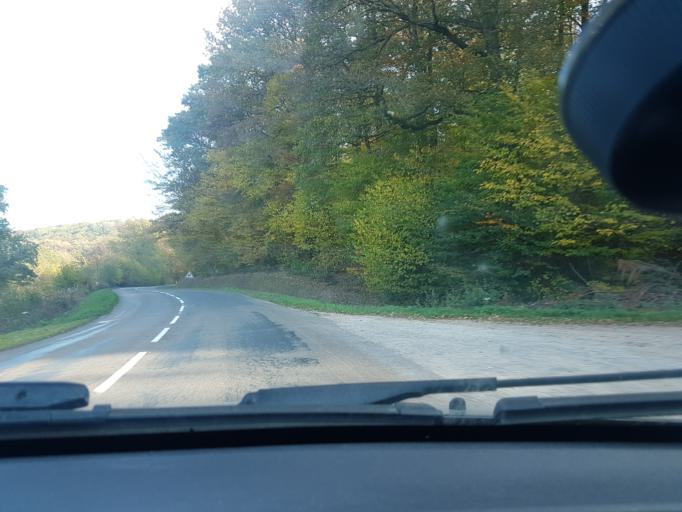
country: FR
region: Franche-Comte
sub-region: Departement de la Haute-Saone
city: Frahier-et-Chatebier
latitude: 47.6786
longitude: 6.7394
